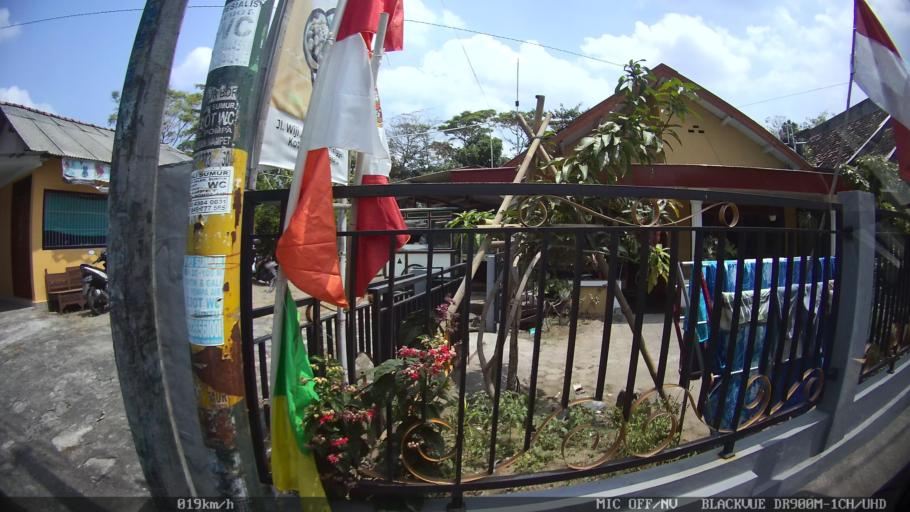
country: ID
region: Daerah Istimewa Yogyakarta
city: Yogyakarta
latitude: -7.8176
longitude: 110.3947
